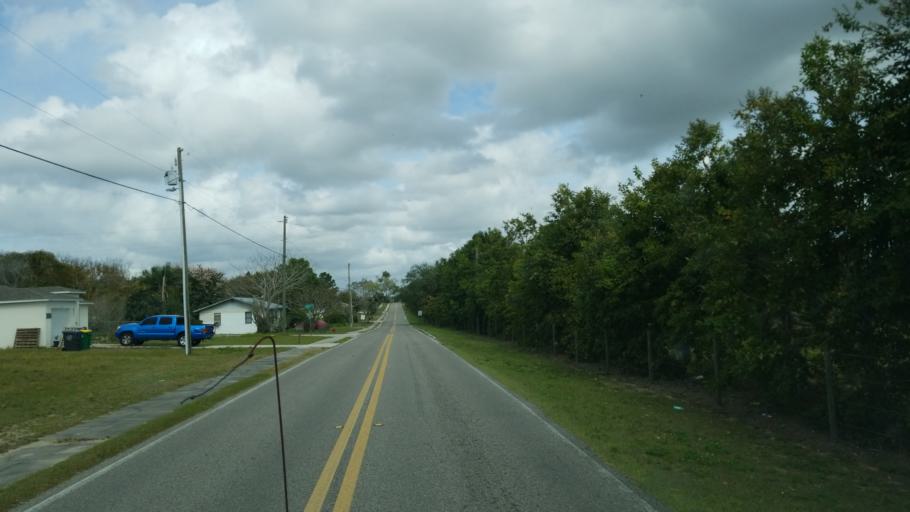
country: US
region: Florida
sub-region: Polk County
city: Dundee
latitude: 28.0272
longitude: -81.6115
